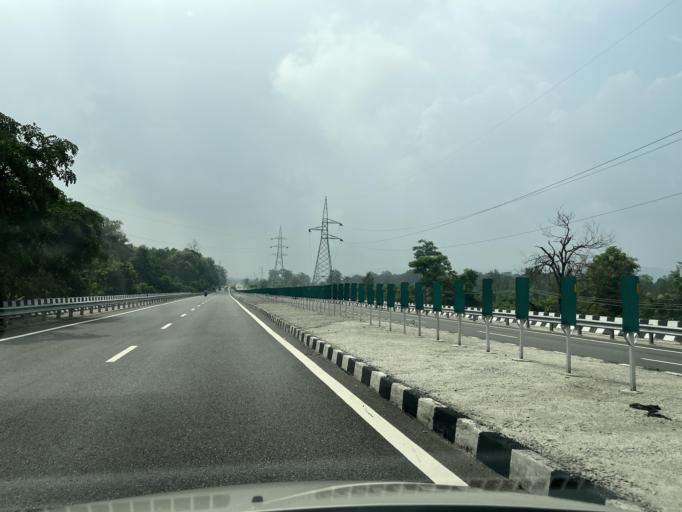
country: IN
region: Uttarakhand
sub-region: Dehradun
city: Raiwala
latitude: 30.0957
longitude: 78.1813
